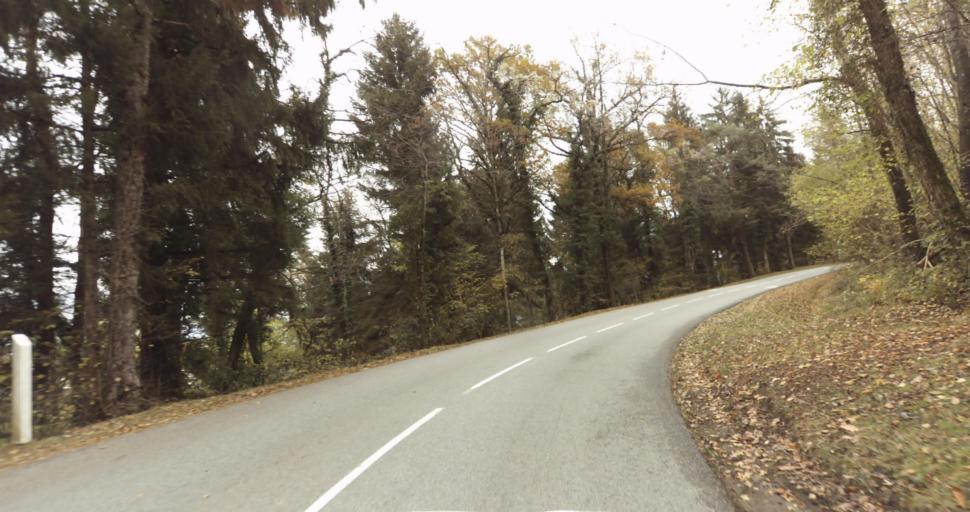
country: FR
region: Rhone-Alpes
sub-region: Departement de la Haute-Savoie
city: Sevrier
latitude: 45.8424
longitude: 6.1389
